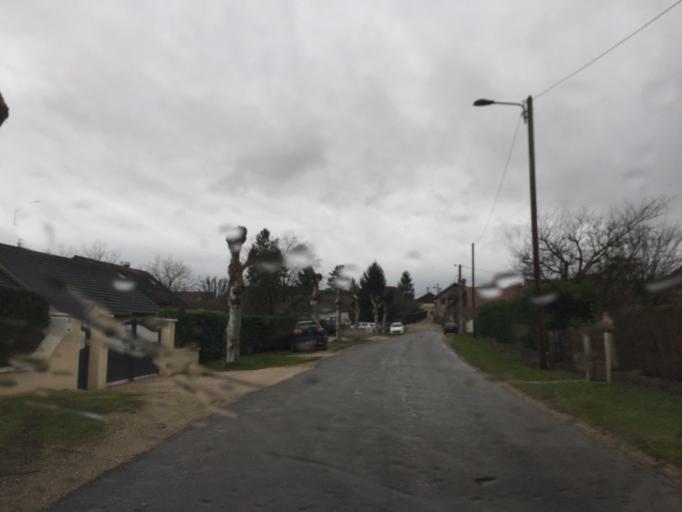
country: FR
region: Franche-Comte
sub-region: Departement du Jura
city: Dole
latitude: 47.1478
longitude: 5.5548
